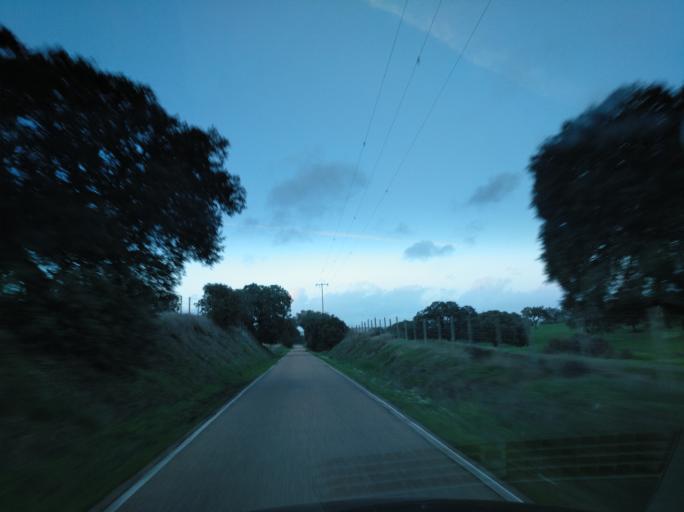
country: PT
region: Portalegre
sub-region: Campo Maior
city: Campo Maior
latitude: 39.0801
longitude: -7.1167
